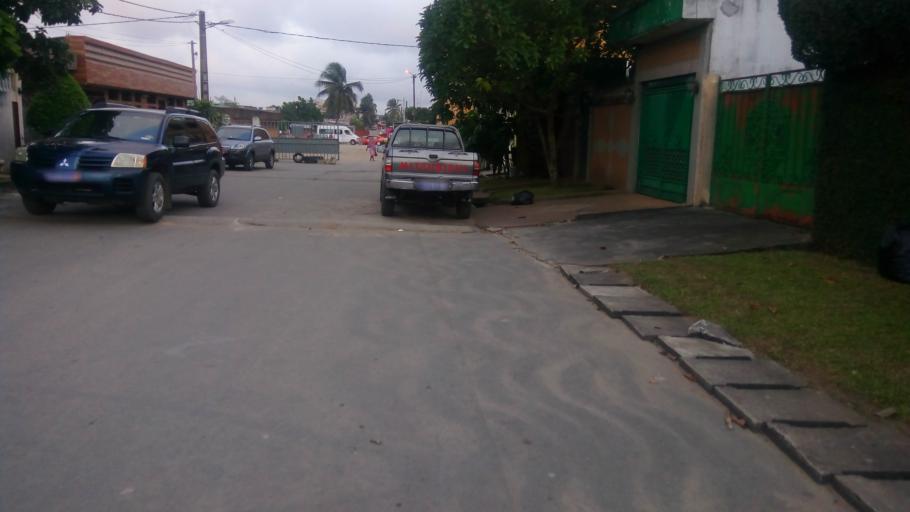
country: CI
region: Lagunes
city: Abobo
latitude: 5.4082
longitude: -3.9892
